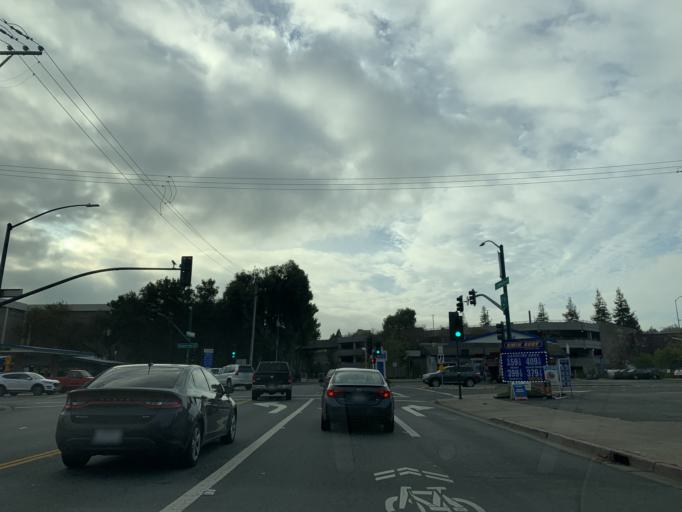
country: US
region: California
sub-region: Contra Costa County
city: Walnut Creek
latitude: 37.8930
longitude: -122.0613
